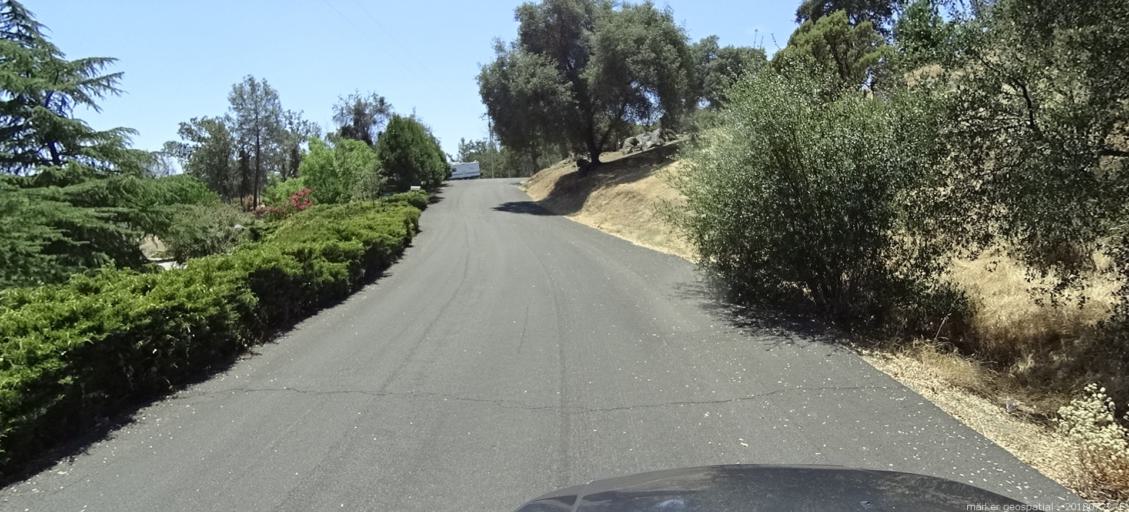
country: US
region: California
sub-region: Madera County
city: Yosemite Lakes
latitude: 37.2075
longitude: -119.7310
